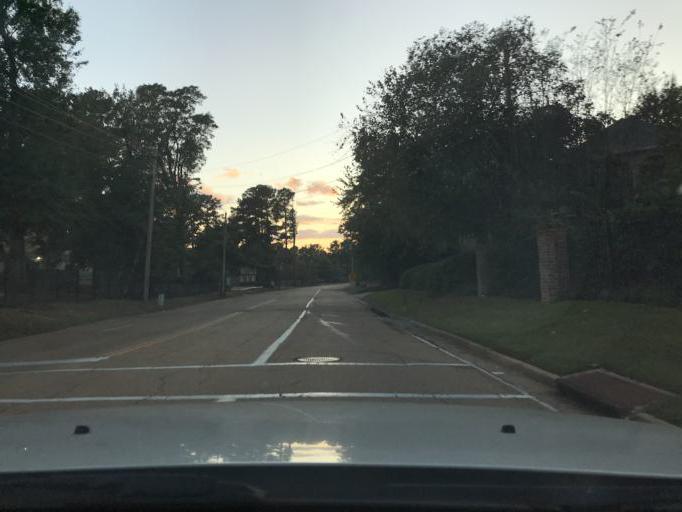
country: US
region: Mississippi
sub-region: Rankin County
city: Flowood
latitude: 32.3470
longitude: -90.1580
